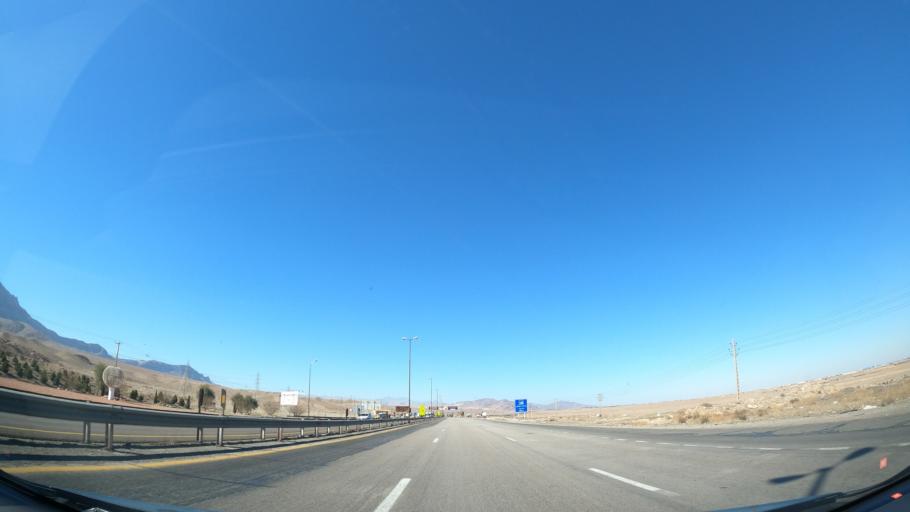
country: IR
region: Isfahan
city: Kashan
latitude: 33.9554
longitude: 51.3587
